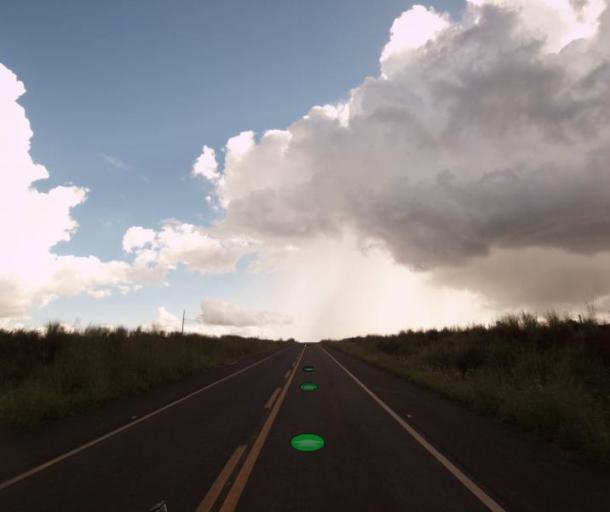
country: BR
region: Goias
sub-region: Itaberai
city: Itaberai
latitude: -15.9892
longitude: -49.7188
